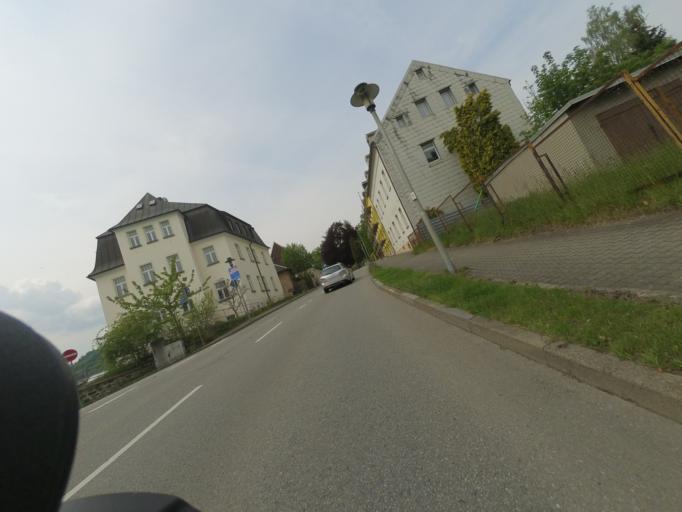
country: DE
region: Saxony
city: Olbernhau
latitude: 50.6587
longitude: 13.3286
